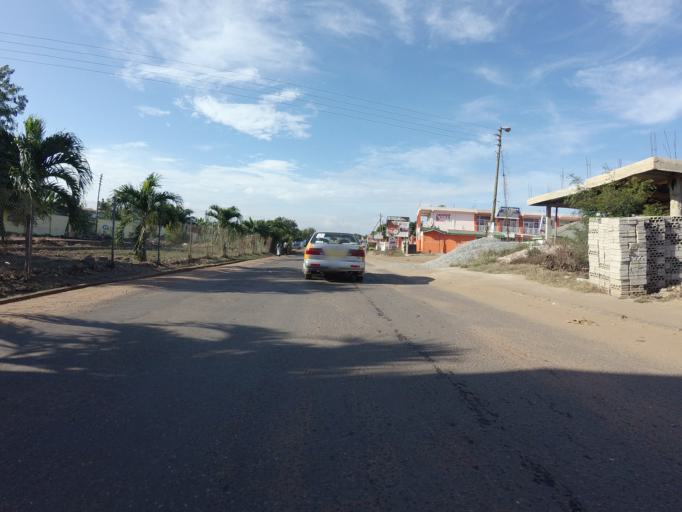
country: GH
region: Greater Accra
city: Tema
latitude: 5.6515
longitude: -0.0643
